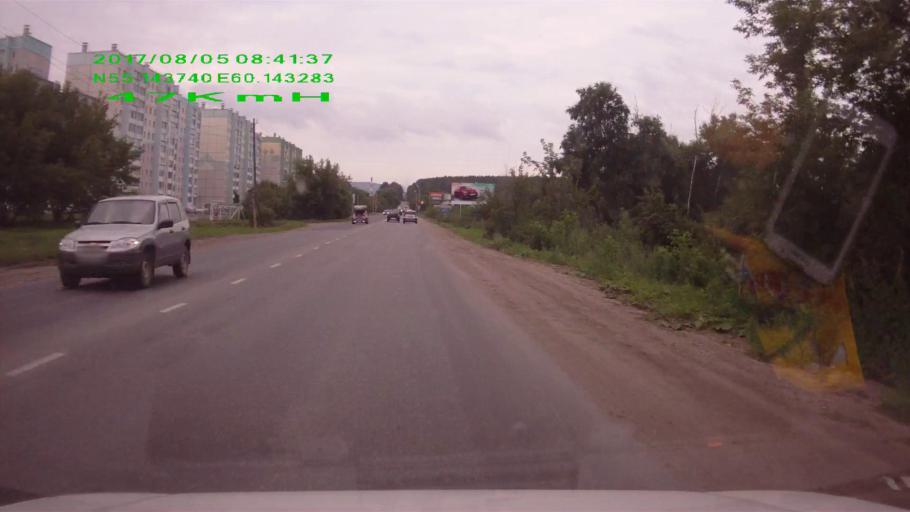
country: RU
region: Chelyabinsk
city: Turgoyak
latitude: 55.1435
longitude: 60.1433
